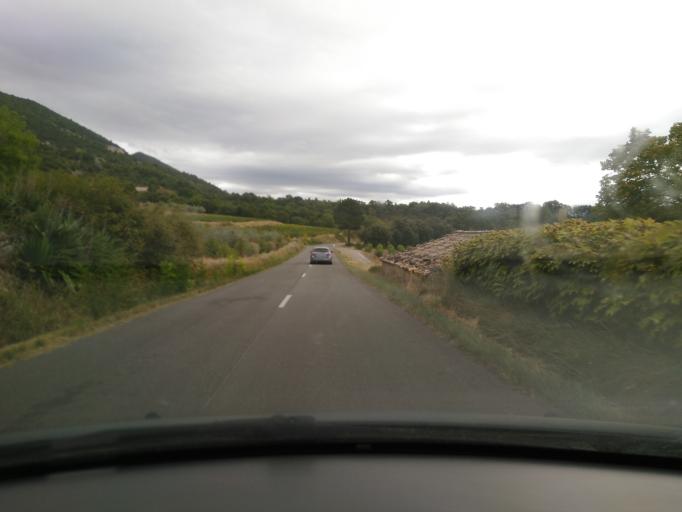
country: FR
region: Rhone-Alpes
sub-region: Departement de la Drome
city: Nyons
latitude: 44.4116
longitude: 5.0718
